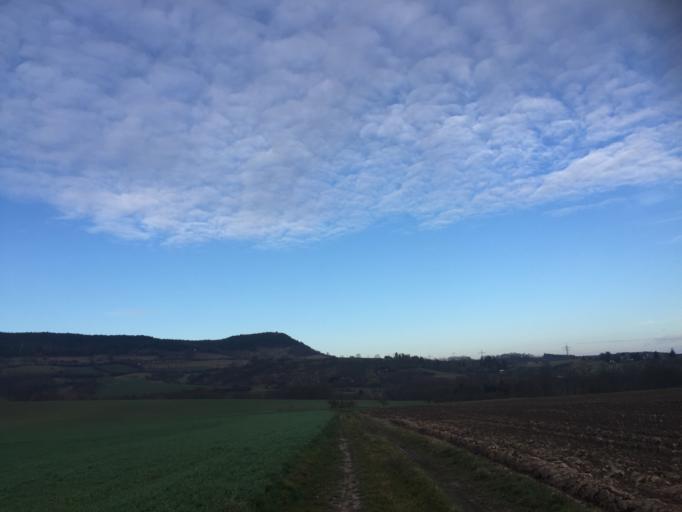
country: DE
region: Thuringia
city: Orlamunde
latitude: 50.7645
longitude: 11.5009
